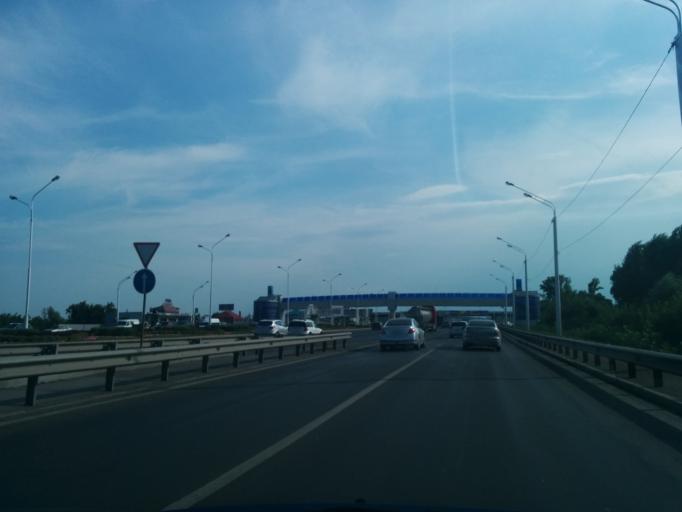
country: RU
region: Bashkortostan
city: Ufa
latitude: 54.7047
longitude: 55.9507
